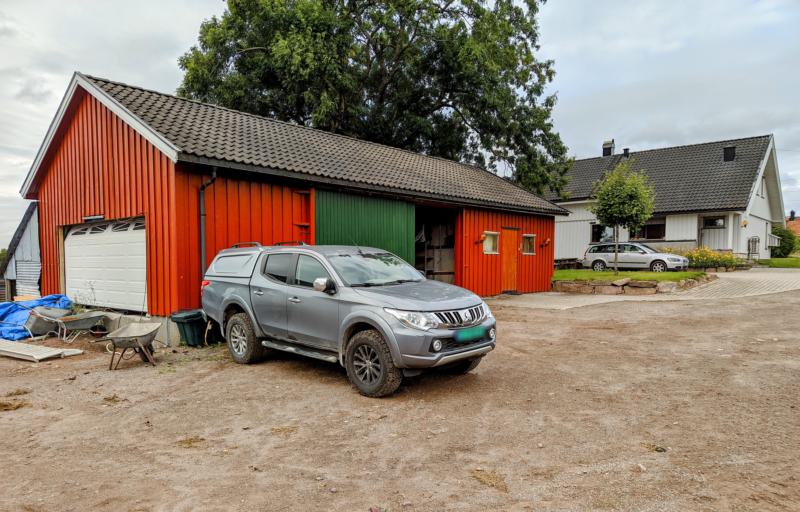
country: NO
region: Vestfold
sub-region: Stokke
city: Stokke
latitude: 59.2377
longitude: 10.2892
